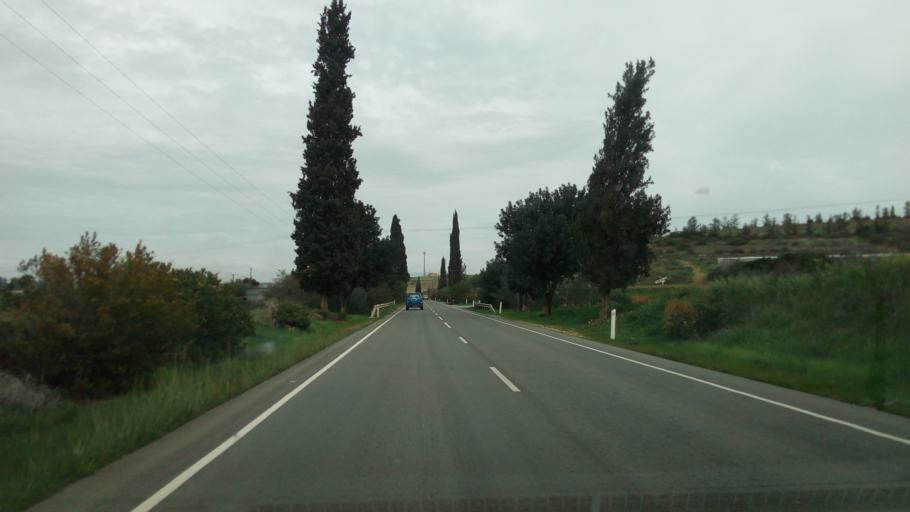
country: CY
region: Lefkosia
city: Astromeritis
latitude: 35.0966
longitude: 32.9679
